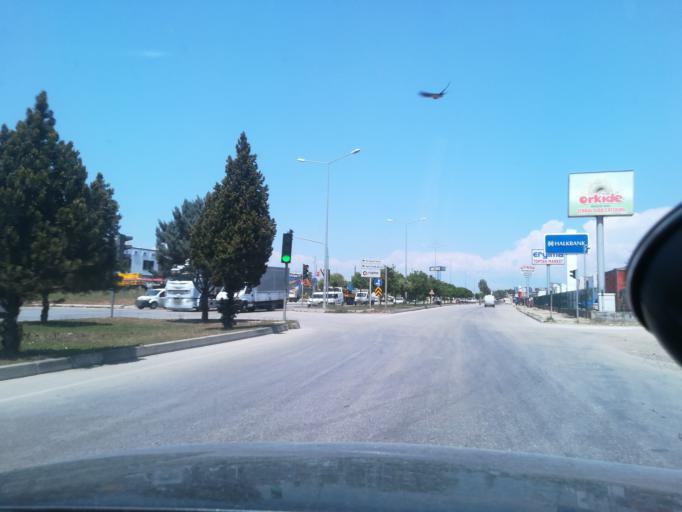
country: TR
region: Adana
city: Seyhan
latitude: 36.9910
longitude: 35.2527
